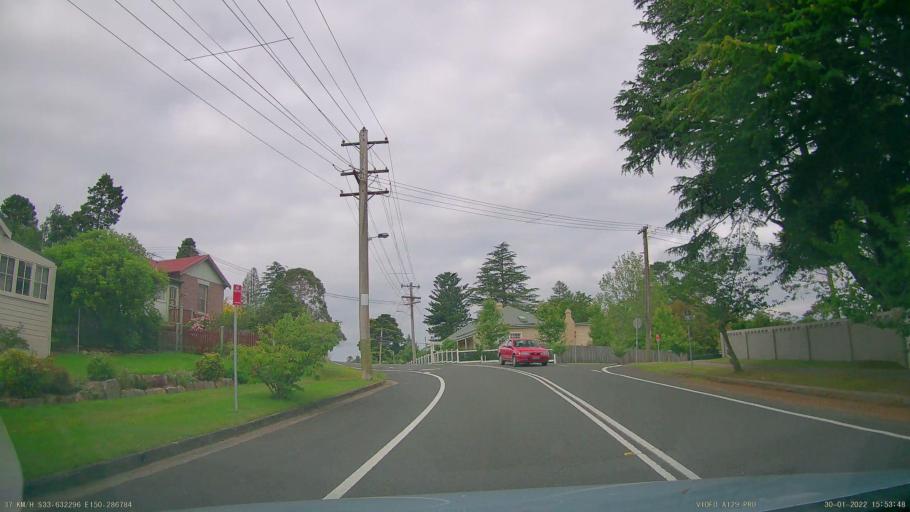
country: AU
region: New South Wales
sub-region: Blue Mountains Municipality
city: Blackheath
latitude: -33.6323
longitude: 150.2869
